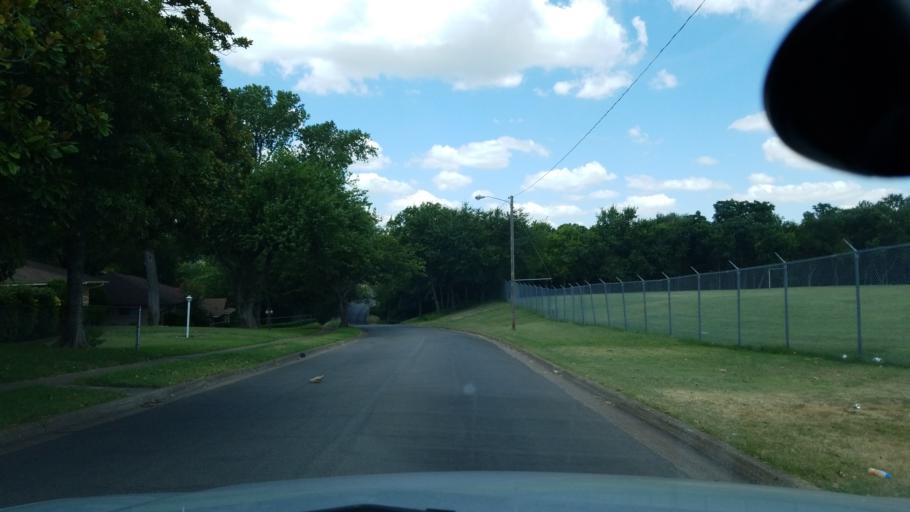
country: US
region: Texas
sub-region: Dallas County
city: Cockrell Hill
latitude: 32.7039
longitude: -96.8426
